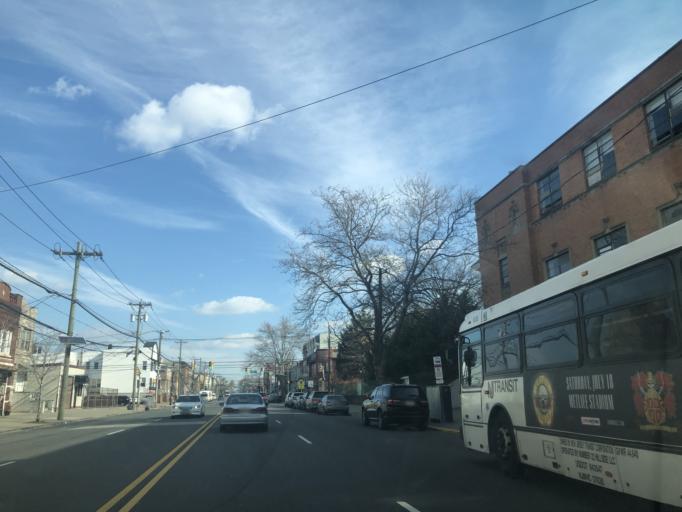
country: US
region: New Jersey
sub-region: Hudson County
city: Bayonne
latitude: 40.6663
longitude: -74.1228
